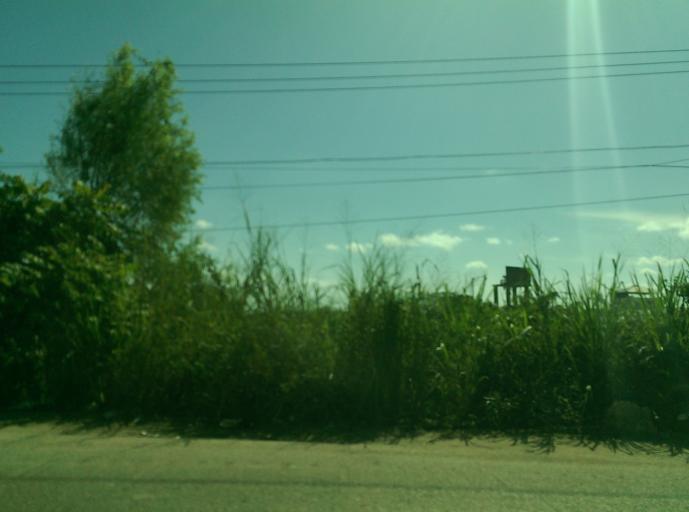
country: MX
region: Tabasco
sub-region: Centro
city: Anacleto Canabal 2da. Seccion
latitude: 17.9827
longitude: -93.0170
